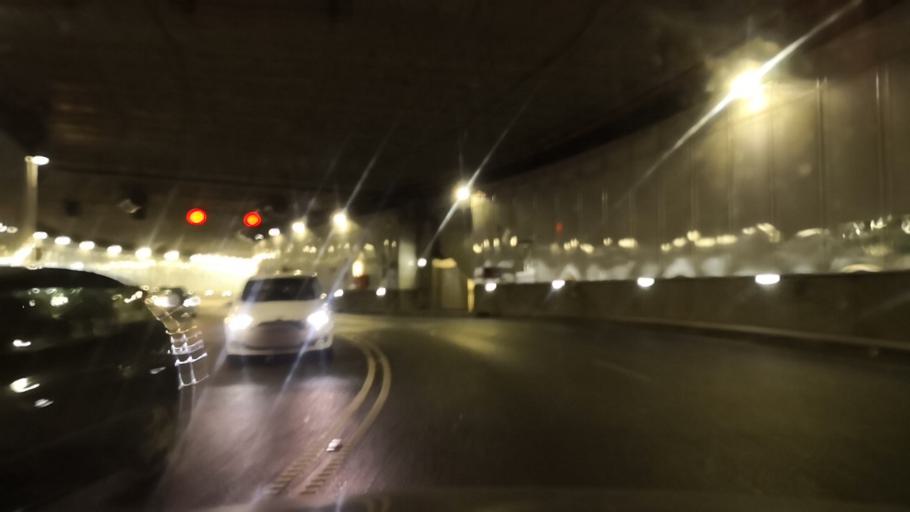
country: ES
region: Galicia
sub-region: Provincia da Coruna
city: A Coruna
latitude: 43.3676
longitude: -8.3965
